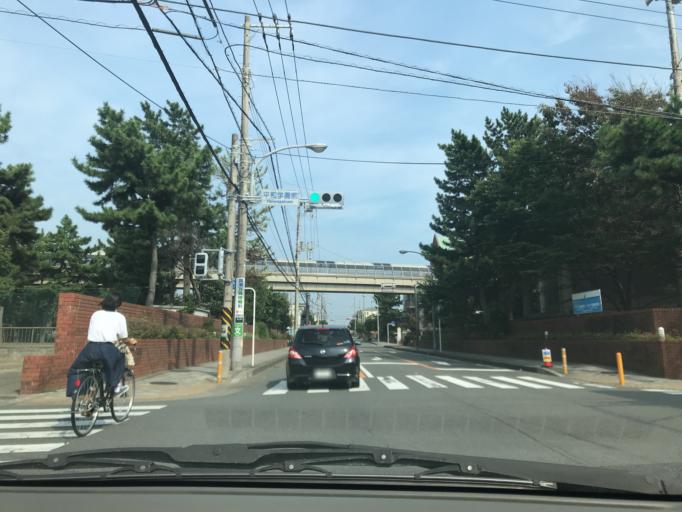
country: JP
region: Kanagawa
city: Chigasaki
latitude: 35.3256
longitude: 139.4313
